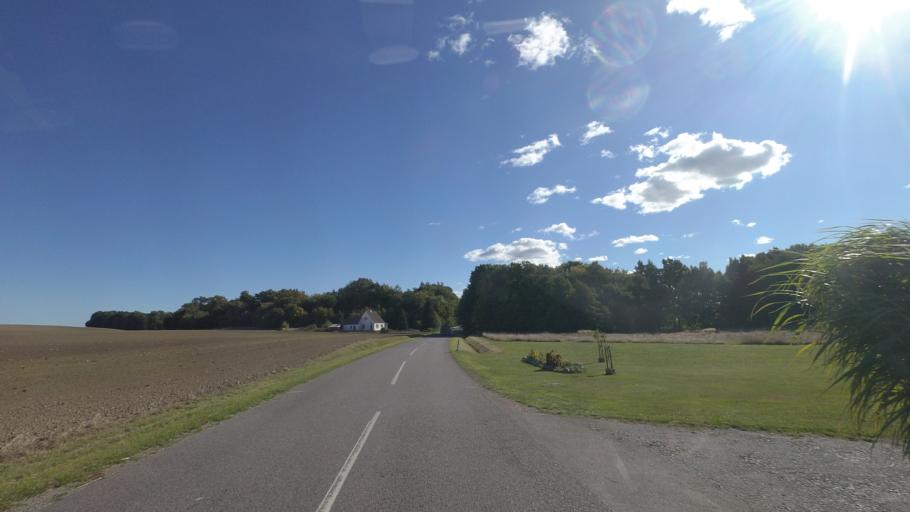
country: DK
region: Capital Region
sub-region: Bornholm Kommune
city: Akirkeby
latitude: 55.1337
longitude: 15.0209
